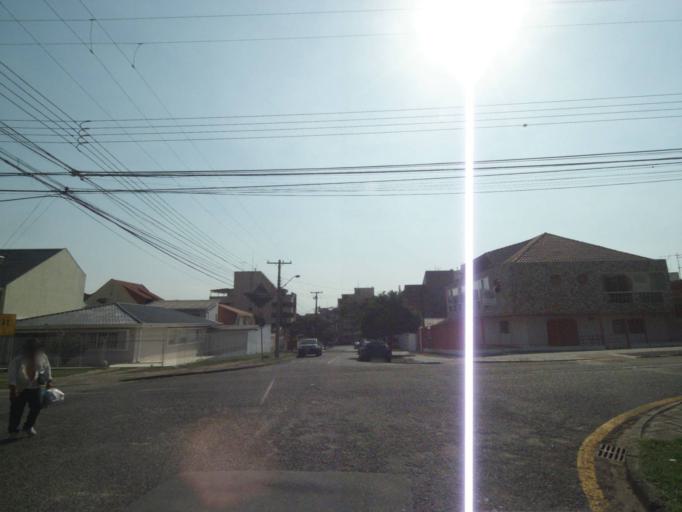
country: BR
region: Parana
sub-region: Curitiba
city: Curitiba
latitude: -25.4630
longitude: -49.2943
